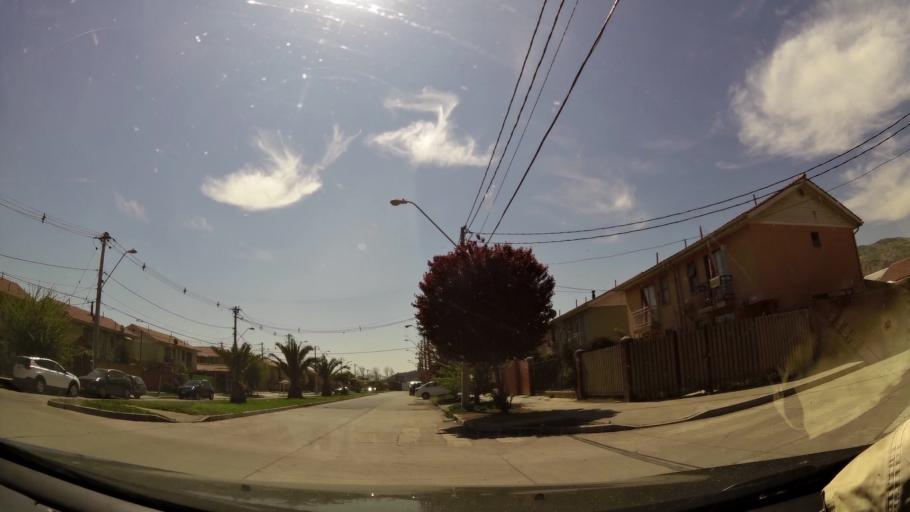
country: CL
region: Santiago Metropolitan
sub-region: Provincia de Santiago
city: Lo Prado
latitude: -33.3956
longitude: -70.7537
